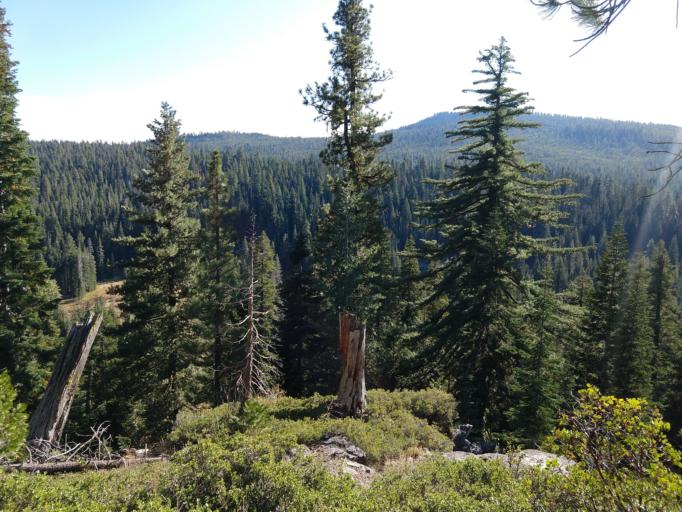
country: US
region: California
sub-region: Plumas County
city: Chester
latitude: 40.4449
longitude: -121.3968
